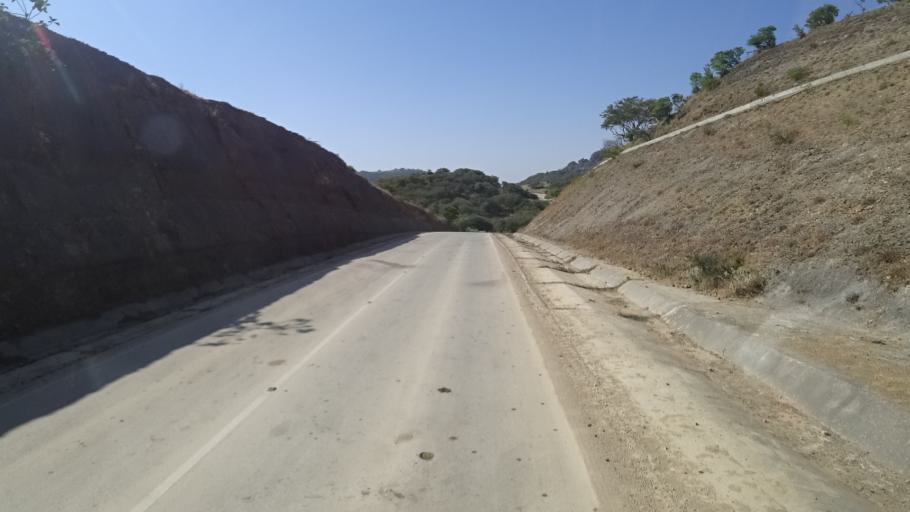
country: OM
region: Zufar
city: Salalah
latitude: 17.0630
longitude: 54.6043
